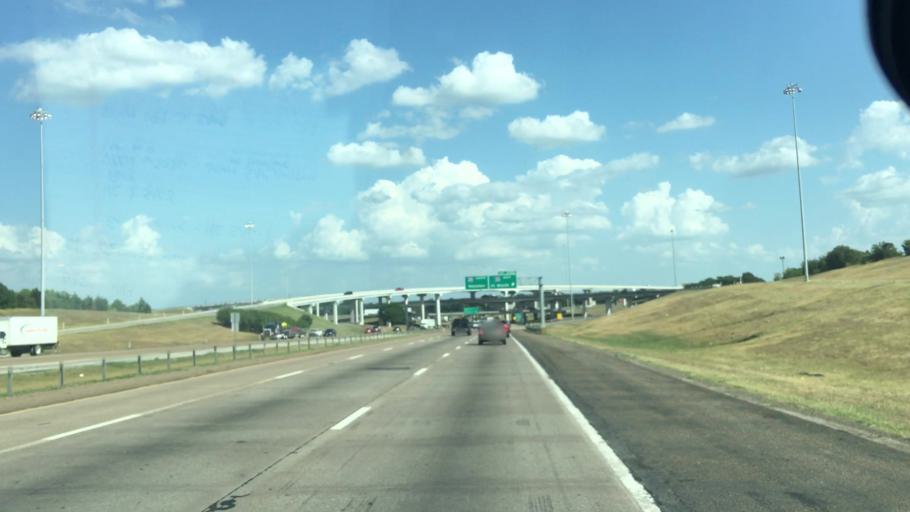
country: US
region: Texas
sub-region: Dallas County
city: Hutchins
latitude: 32.6654
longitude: -96.7301
